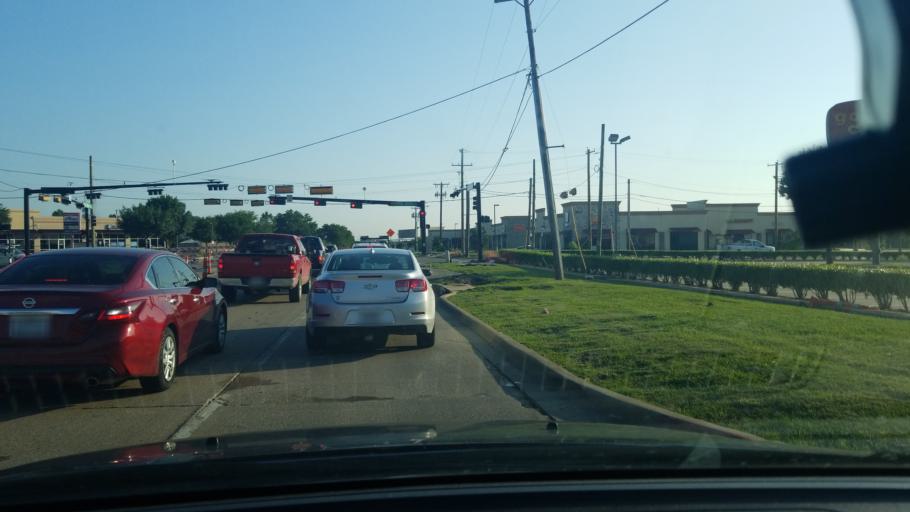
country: US
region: Texas
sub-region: Dallas County
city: Mesquite
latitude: 32.7982
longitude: -96.6339
